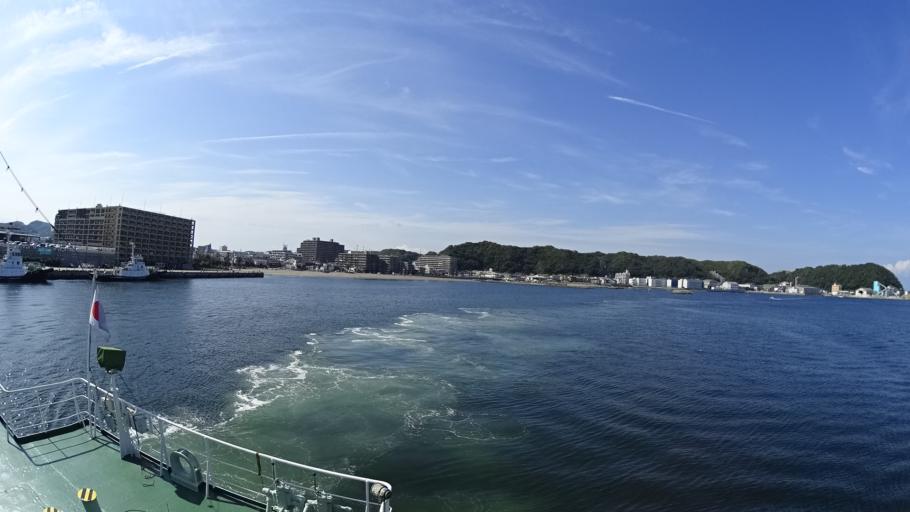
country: JP
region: Kanagawa
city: Yokosuka
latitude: 35.2217
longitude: 139.7153
